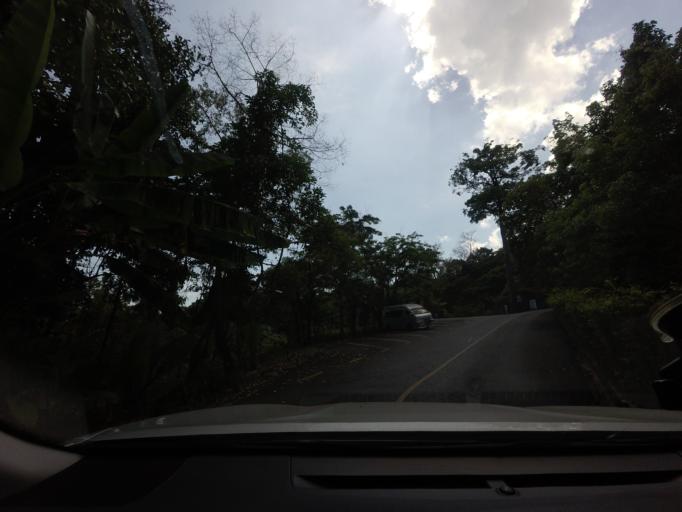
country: TH
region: Phuket
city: Mueang Phuket
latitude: 7.8768
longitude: 98.3522
